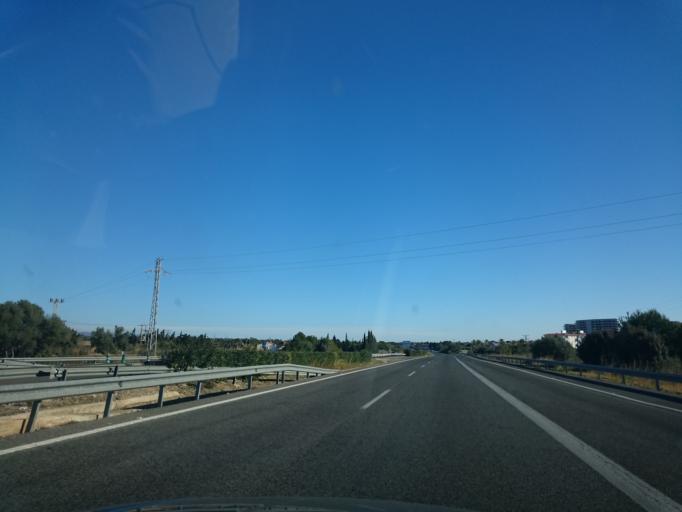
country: ES
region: Catalonia
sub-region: Provincia de Tarragona
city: L'Ampolla
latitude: 40.8129
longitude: 0.7044
